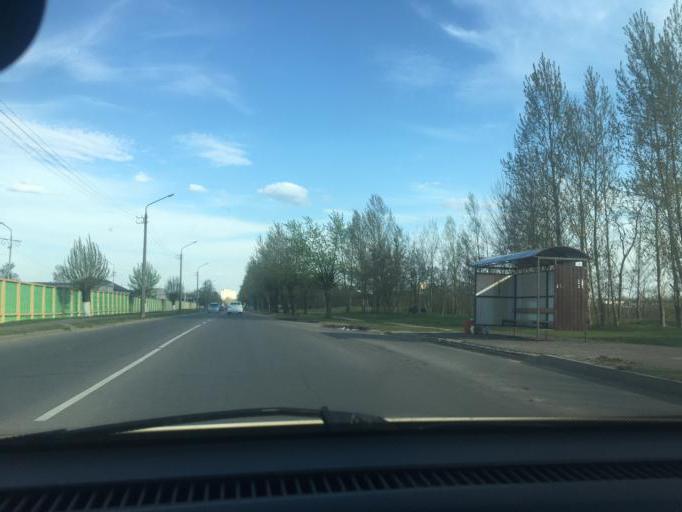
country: BY
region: Mogilev
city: Babruysk
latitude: 53.1571
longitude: 29.1748
